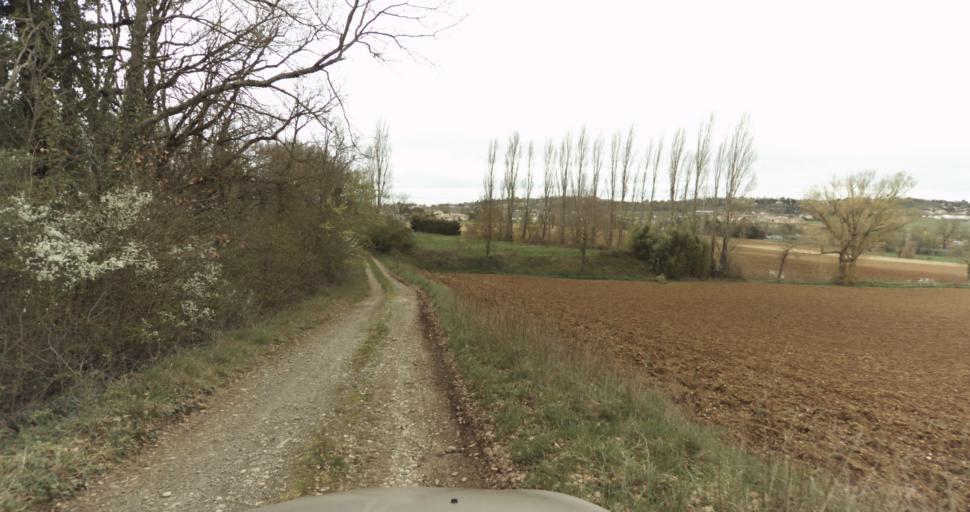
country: FR
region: Midi-Pyrenees
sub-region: Departement du Tarn
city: Puygouzon
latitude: 43.8835
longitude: 2.1636
